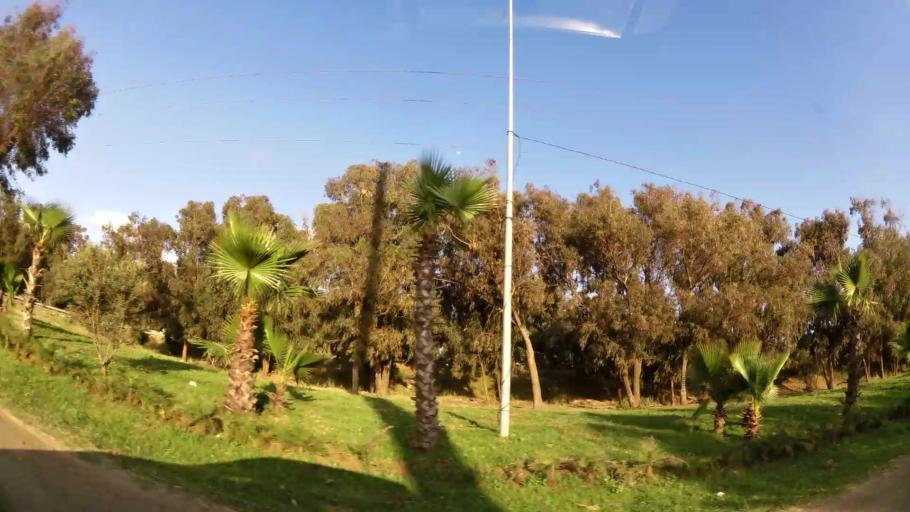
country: MA
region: Rabat-Sale-Zemmour-Zaer
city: Sale
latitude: 34.1047
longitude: -6.7560
